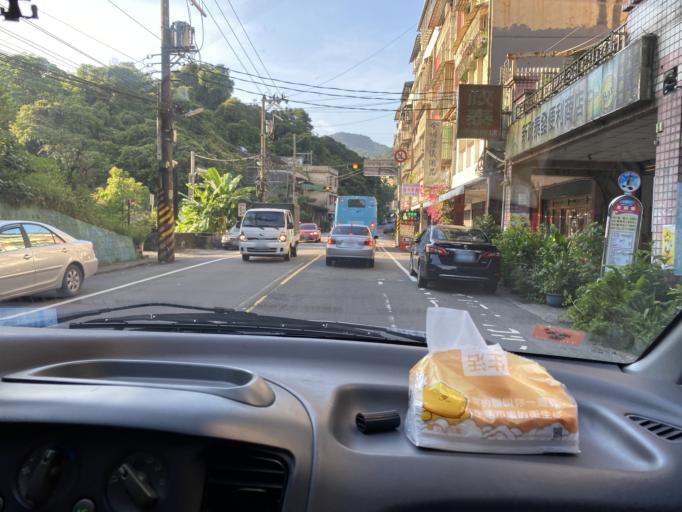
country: TW
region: Taiwan
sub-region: Keelung
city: Keelung
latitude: 25.0950
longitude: 121.7389
